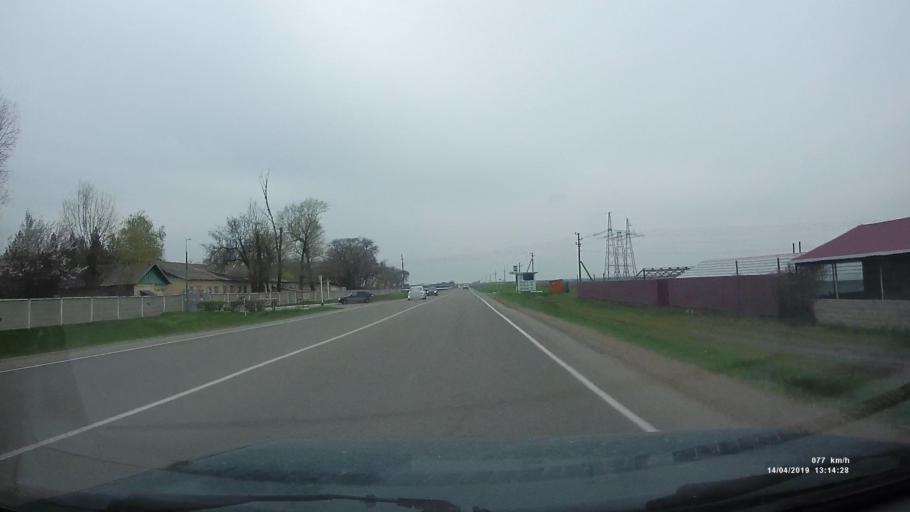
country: RU
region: Rostov
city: Kuleshovka
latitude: 47.0904
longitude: 39.6089
